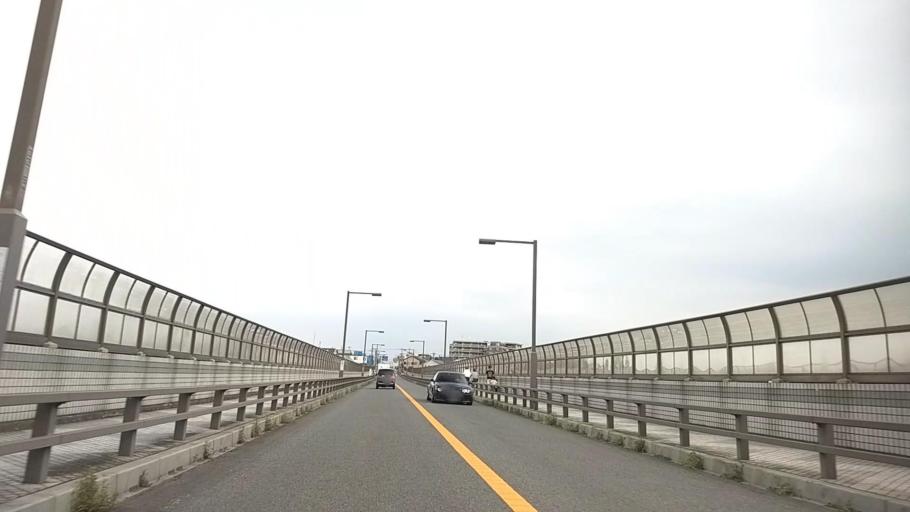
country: JP
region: Kanagawa
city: Minami-rinkan
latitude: 35.4742
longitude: 139.4186
